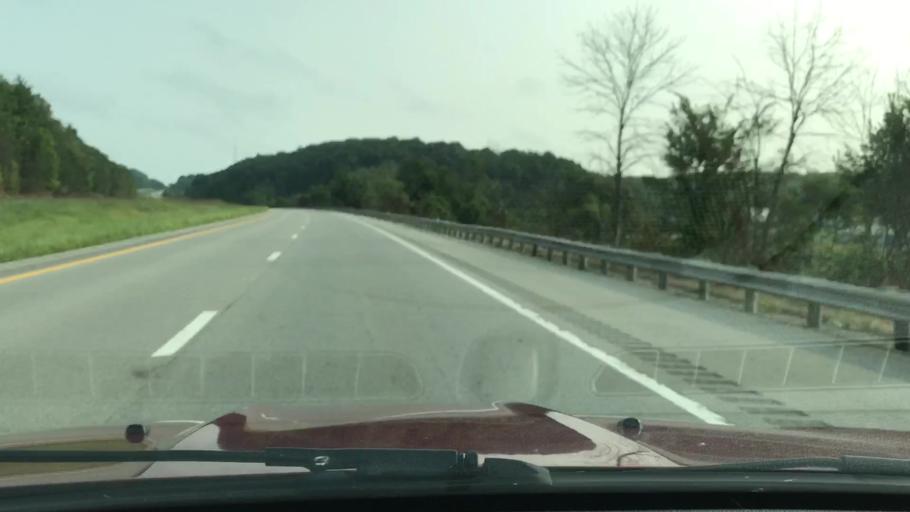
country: US
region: Ohio
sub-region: Guernsey County
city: Byesville
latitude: 39.8793
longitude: -81.5331
